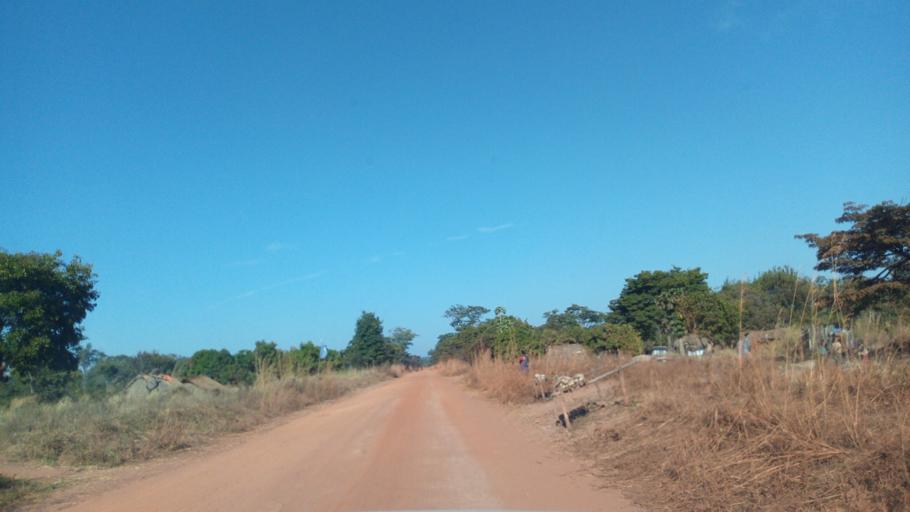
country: ZM
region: Luapula
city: Mwense
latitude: -10.6021
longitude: 28.4230
